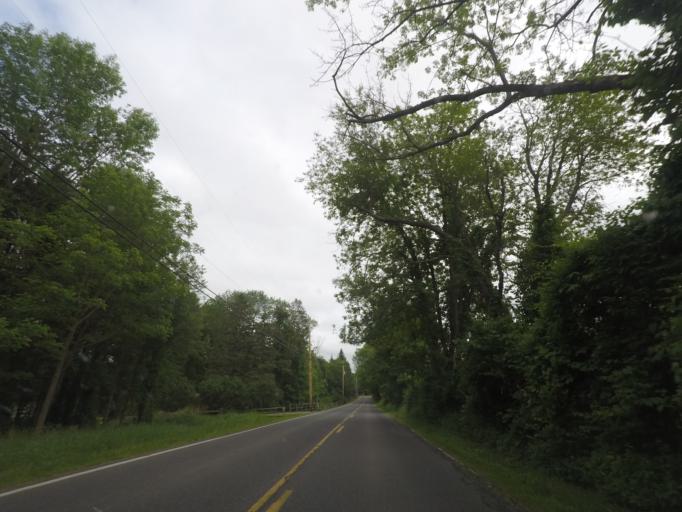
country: US
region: New York
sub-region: Dutchess County
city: Pine Plains
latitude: 41.9730
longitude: -73.5042
